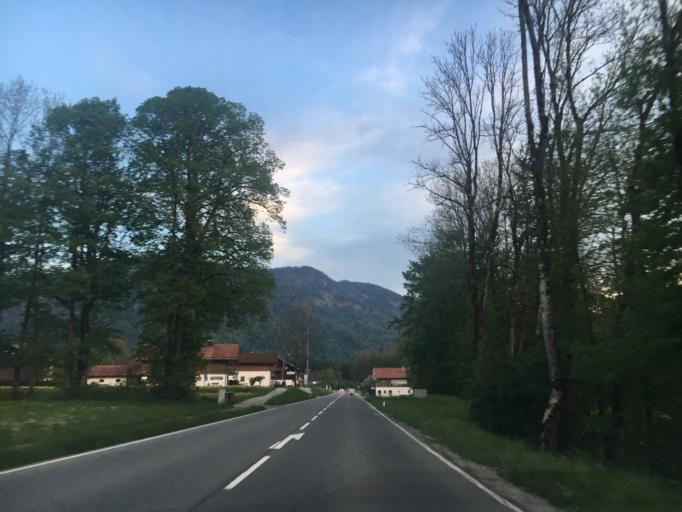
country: DE
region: Bavaria
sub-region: Upper Bavaria
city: Lenggries
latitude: 47.6393
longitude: 11.5936
